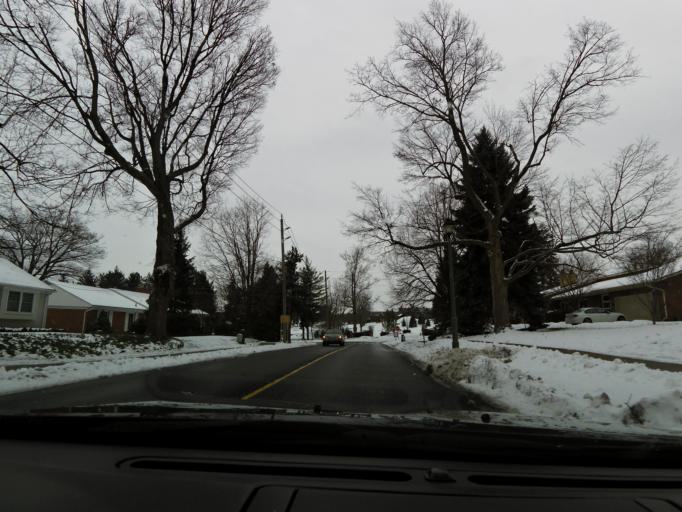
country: CA
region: Ontario
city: Ancaster
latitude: 43.2222
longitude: -79.9774
